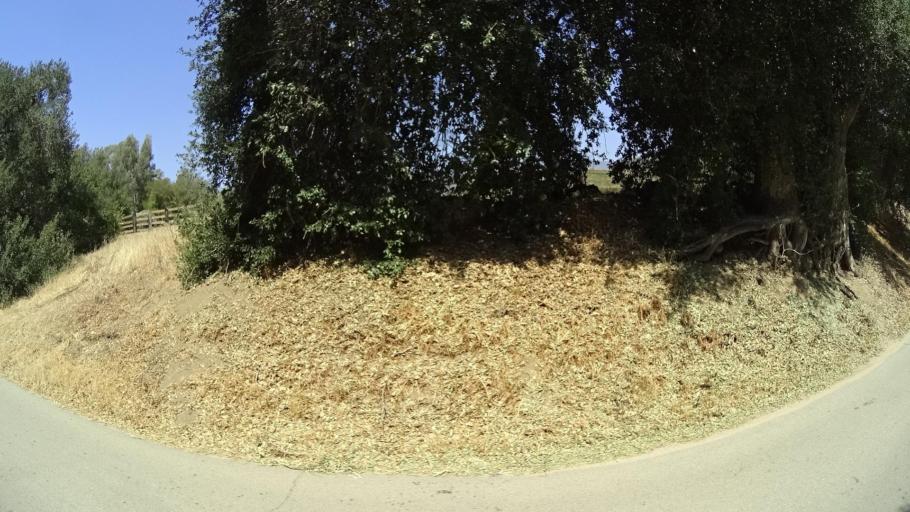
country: US
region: California
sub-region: San Diego County
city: Fallbrook
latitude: 33.4524
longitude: -117.3069
